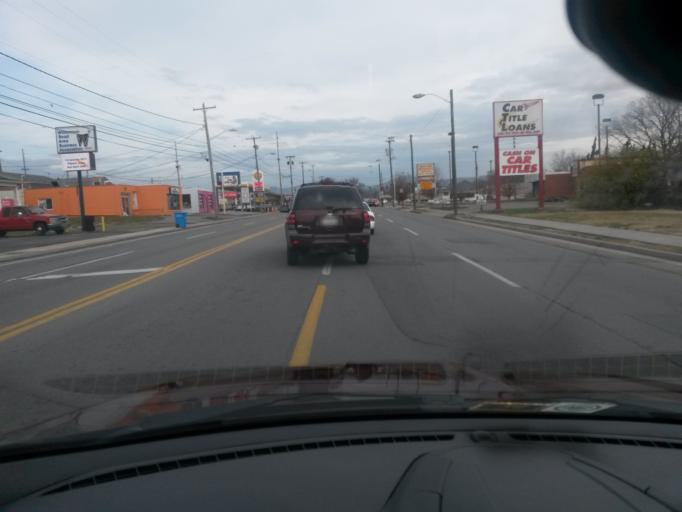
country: US
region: Virginia
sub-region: Roanoke County
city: Hollins
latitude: 37.3152
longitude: -79.9540
